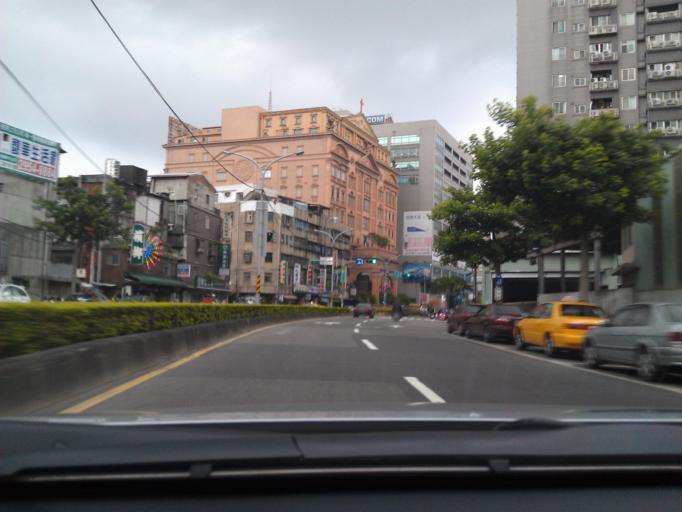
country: TW
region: Taipei
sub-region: Taipei
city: Banqiao
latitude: 25.0236
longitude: 121.4787
